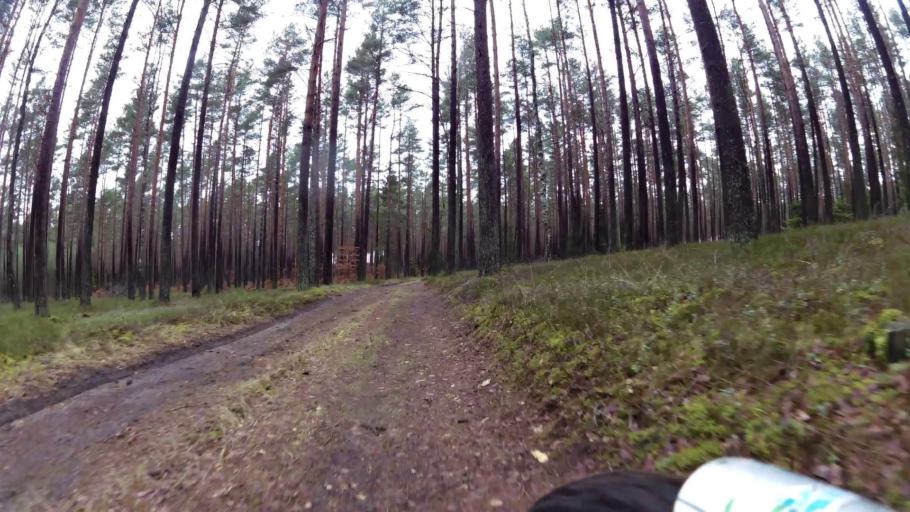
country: PL
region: Pomeranian Voivodeship
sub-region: Powiat bytowski
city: Borzytuchom
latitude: 54.2639
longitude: 17.3564
